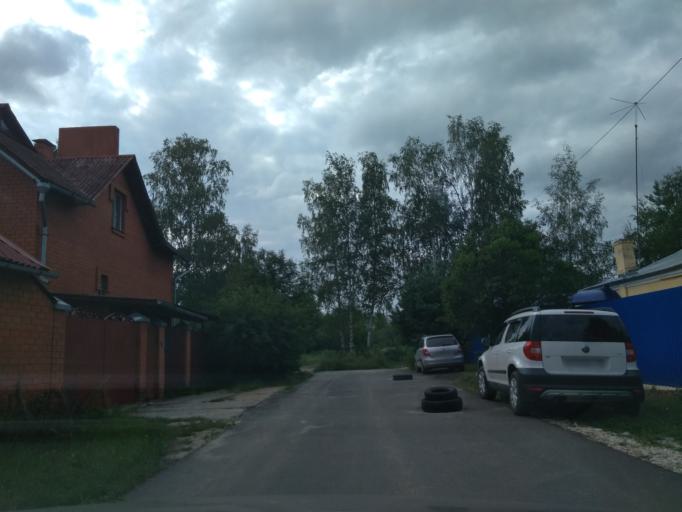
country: RU
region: Moskovskaya
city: Kabanovo
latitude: 55.7851
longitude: 38.9219
